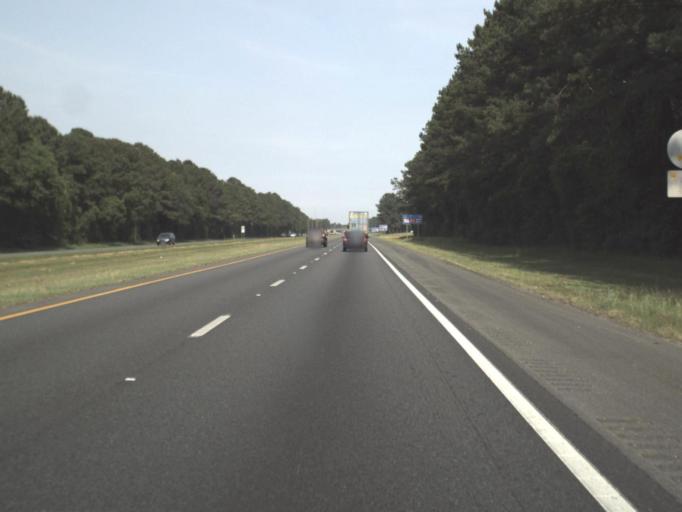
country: US
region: Florida
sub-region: Baker County
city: Macclenny
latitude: 30.2597
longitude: -82.1365
